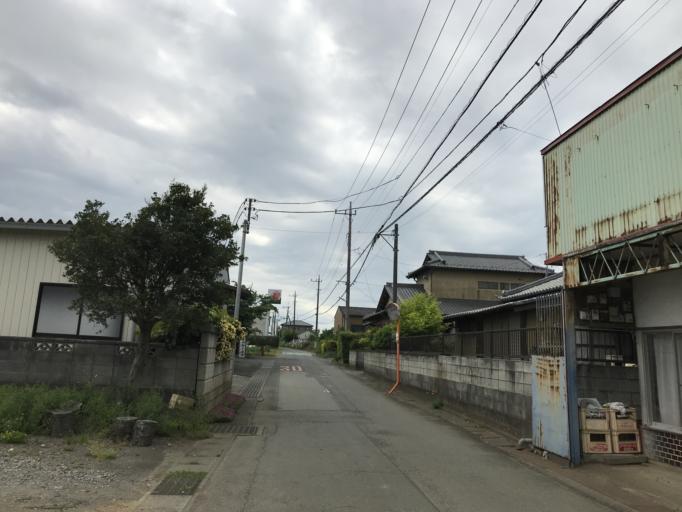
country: JP
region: Ibaraki
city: Mitsukaido
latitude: 36.0266
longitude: 140.0318
